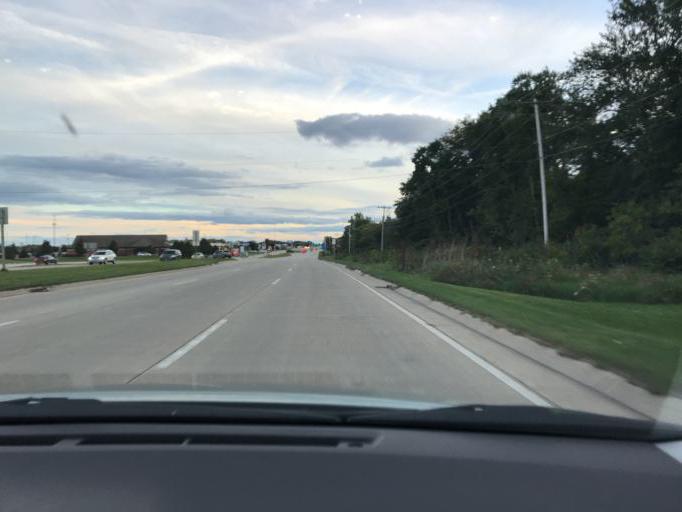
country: US
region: Wisconsin
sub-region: Kenosha County
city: Somers
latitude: 42.6022
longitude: -87.8793
